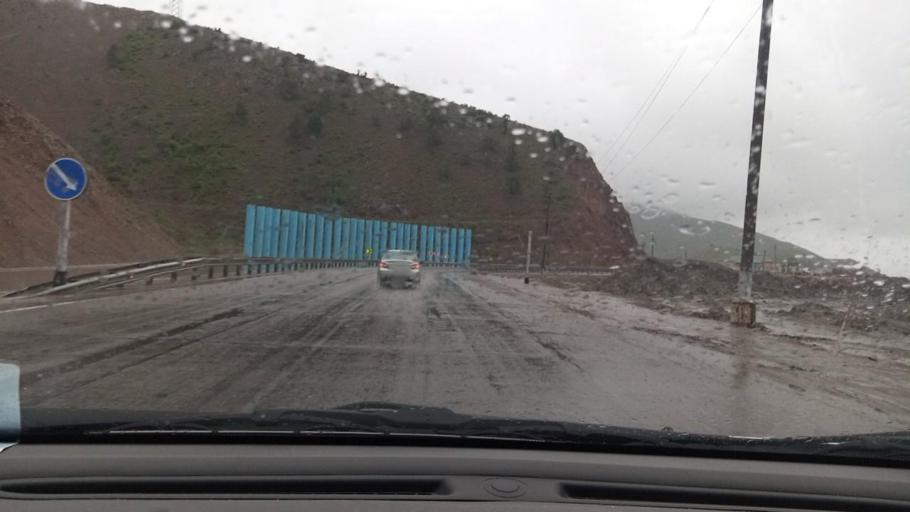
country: UZ
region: Toshkent
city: Angren
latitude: 41.0935
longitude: 70.5309
